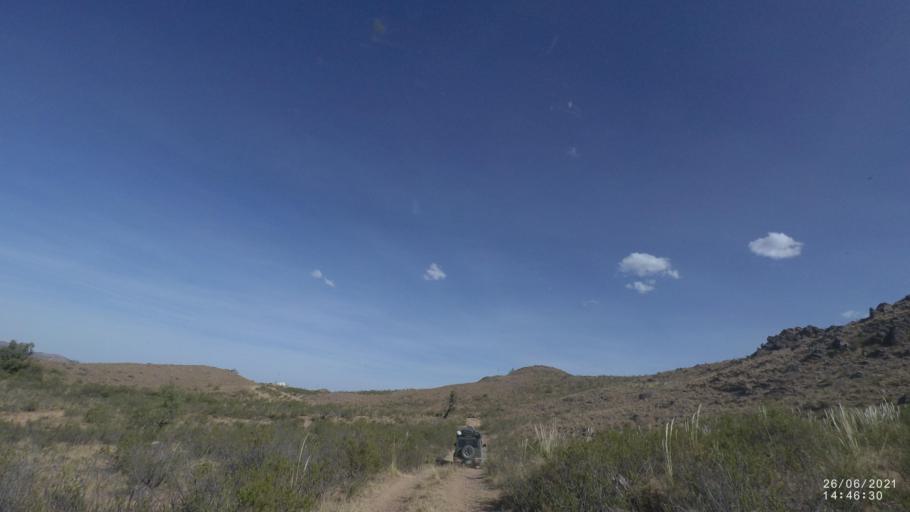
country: BO
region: Cochabamba
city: Mizque
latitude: -17.9161
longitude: -65.6259
